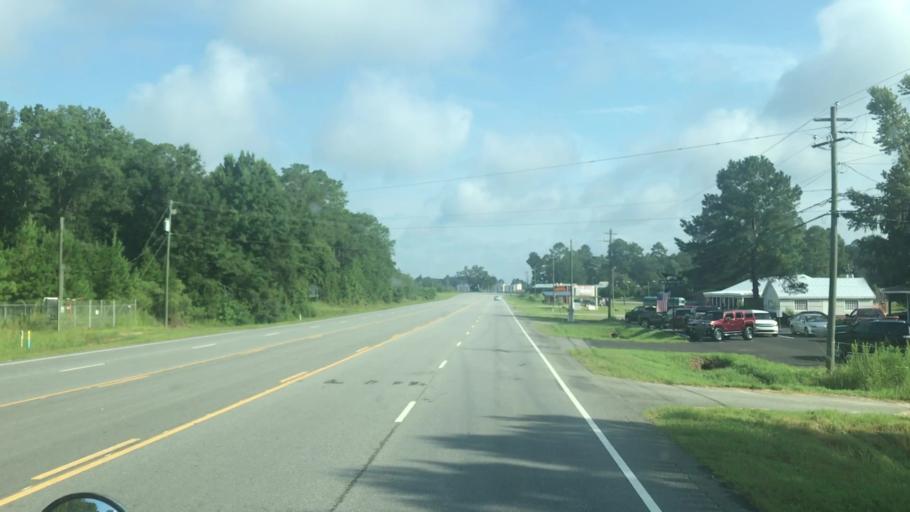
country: US
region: Georgia
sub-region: Decatur County
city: Bainbridge
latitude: 30.8735
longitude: -84.5624
